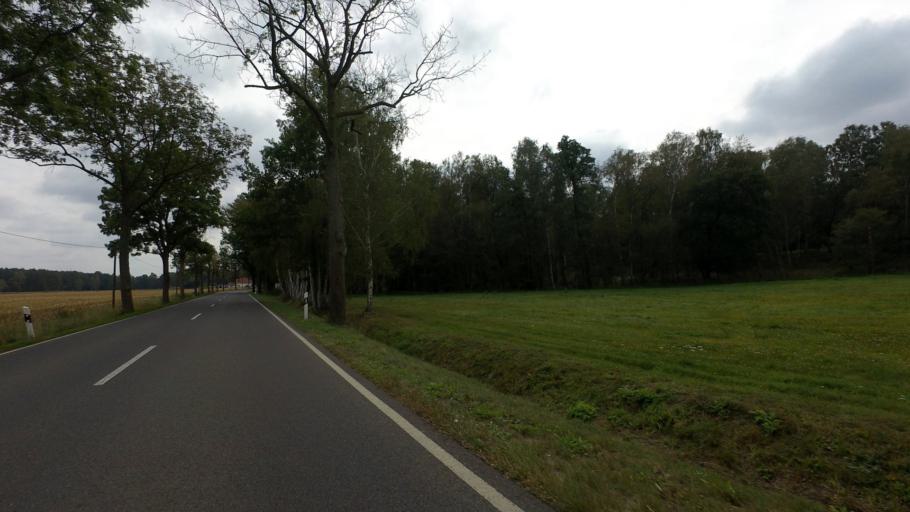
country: DE
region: Brandenburg
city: Luckau
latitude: 51.7999
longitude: 13.6830
